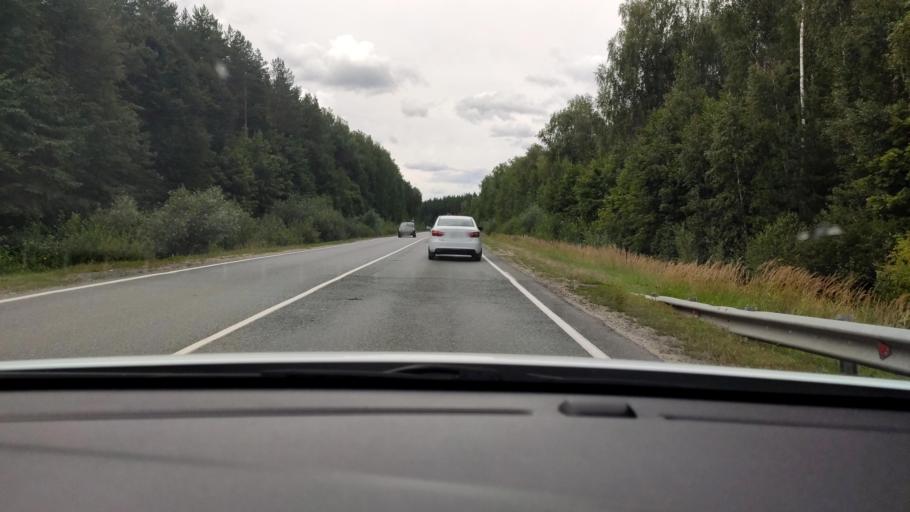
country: RU
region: Tatarstan
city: Aysha
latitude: 55.8953
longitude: 48.5663
